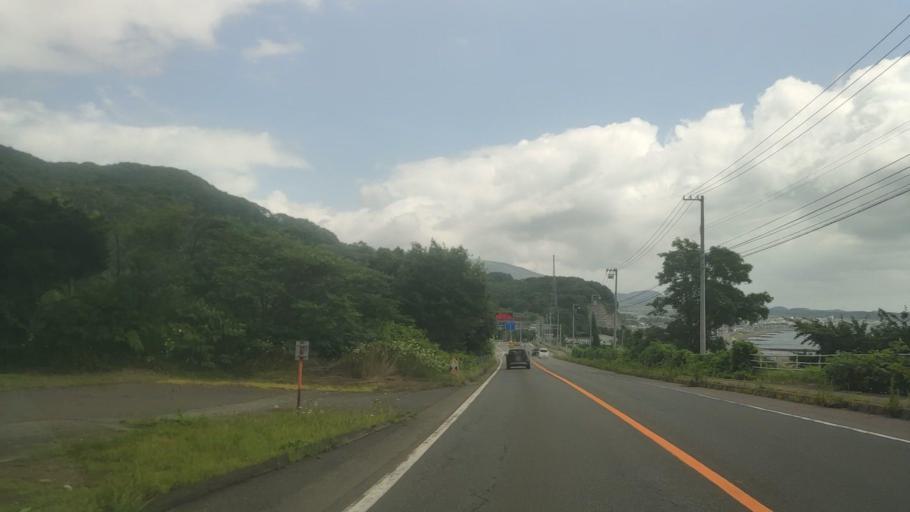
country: JP
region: Hokkaido
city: Date
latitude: 42.5577
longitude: 140.7483
